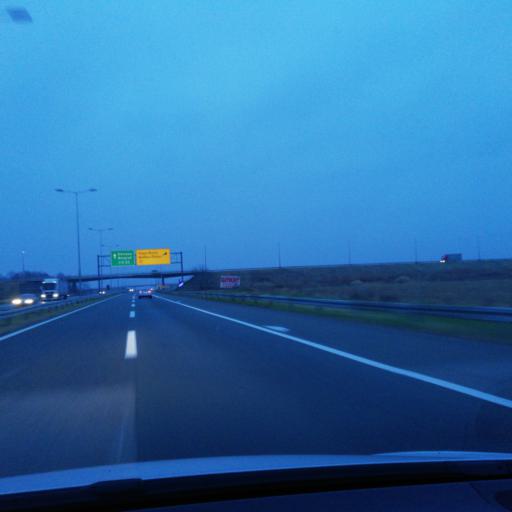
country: RS
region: Autonomna Pokrajina Vojvodina
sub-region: Sremski Okrug
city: Ruma
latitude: 44.9640
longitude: 19.8037
